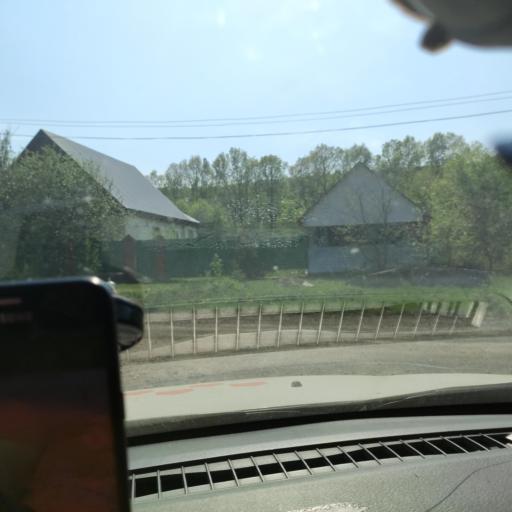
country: RU
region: Bashkortostan
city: Kabakovo
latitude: 54.6310
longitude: 56.1007
